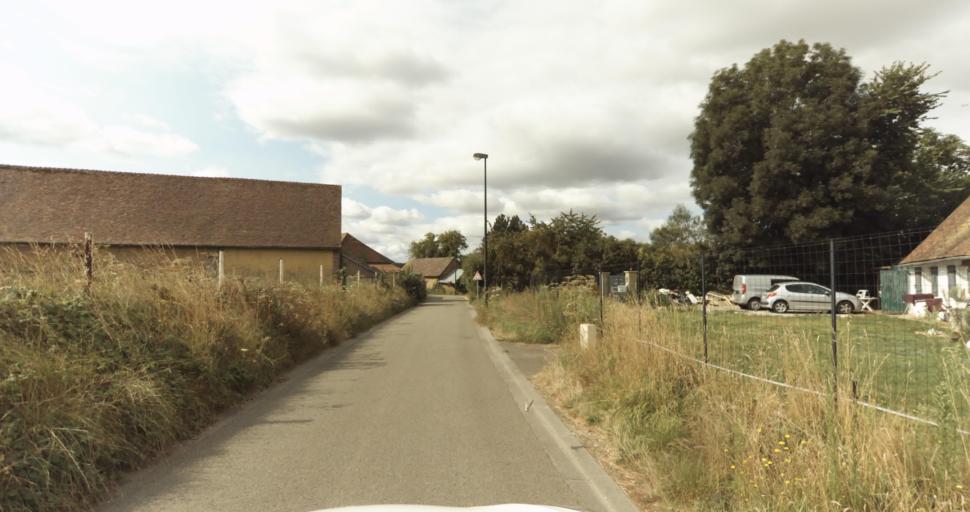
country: FR
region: Haute-Normandie
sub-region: Departement de l'Eure
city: Tillieres-sur-Avre
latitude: 48.7791
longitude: 1.1042
